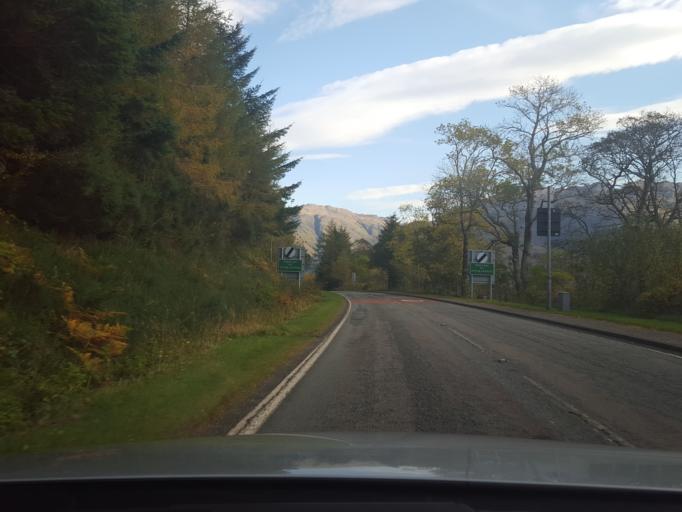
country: GB
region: Scotland
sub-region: Highland
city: Fort William
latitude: 57.2338
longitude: -5.4157
